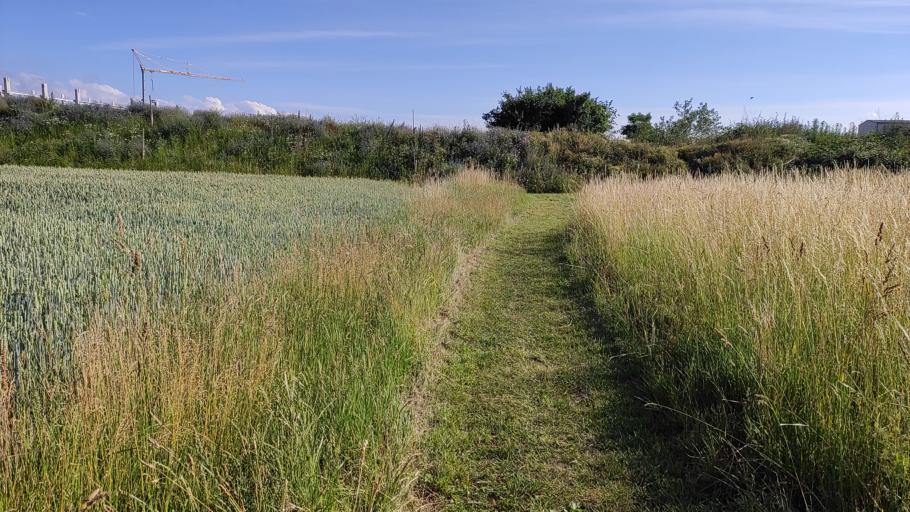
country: DE
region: Baden-Wuerttemberg
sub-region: Freiburg Region
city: Merdingen
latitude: 47.9916
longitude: 7.6536
